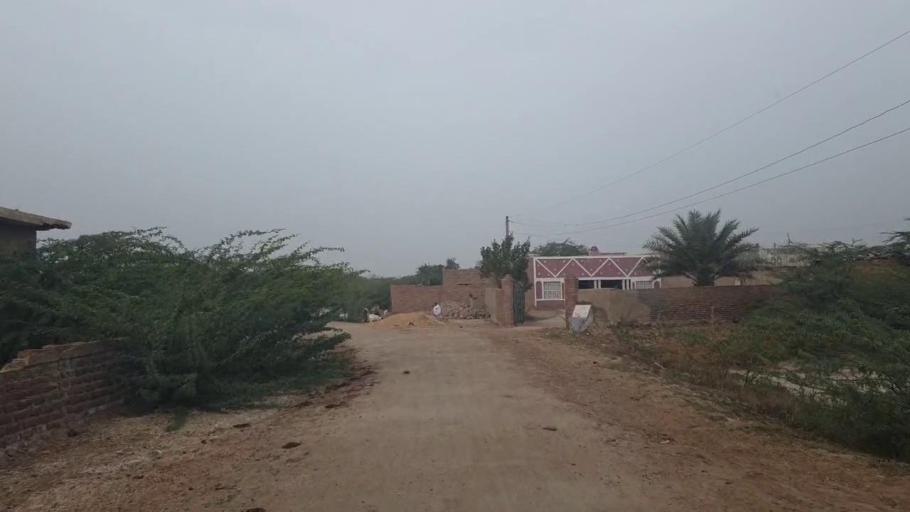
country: PK
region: Sindh
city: Berani
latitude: 25.8095
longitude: 68.7341
